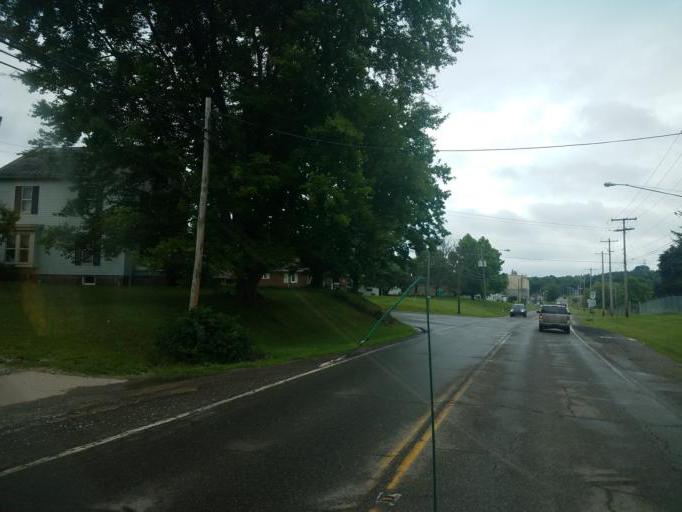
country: US
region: Ohio
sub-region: Carroll County
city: Carrollton
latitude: 40.5879
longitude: -81.0817
